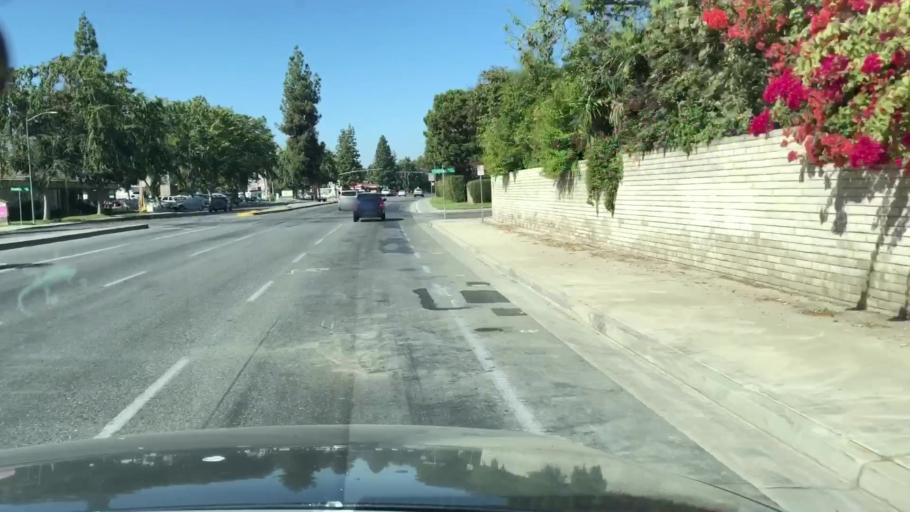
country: US
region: California
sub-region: Kern County
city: Greenacres
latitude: 35.3349
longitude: -119.0719
